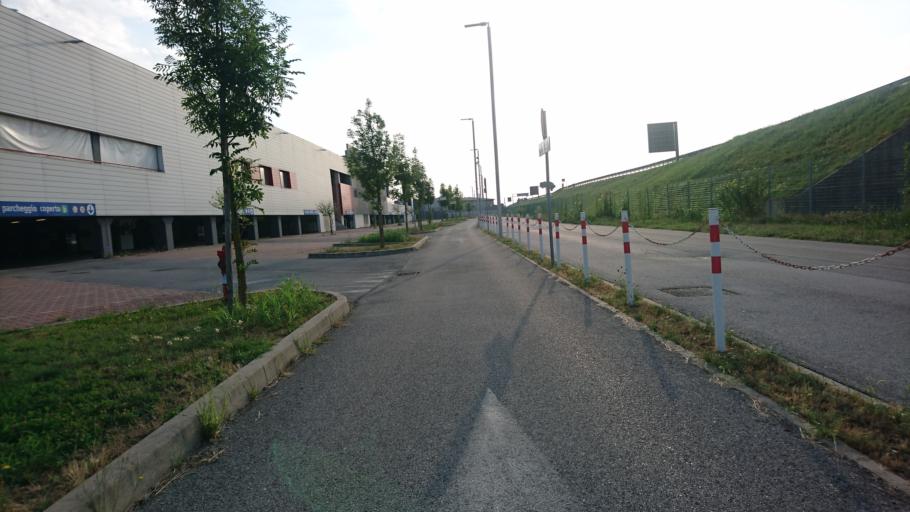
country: IT
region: Veneto
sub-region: Provincia di Padova
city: San Vito
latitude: 45.4241
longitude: 11.9643
